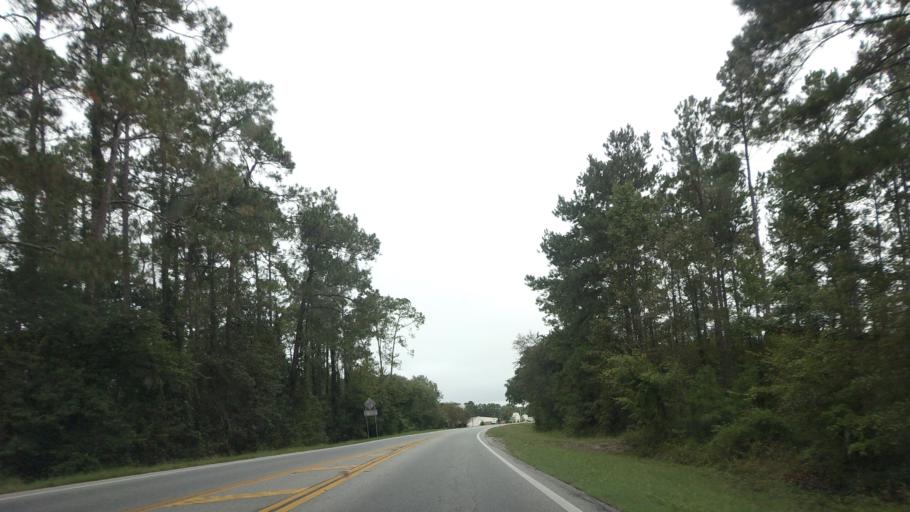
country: US
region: Georgia
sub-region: Berrien County
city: Nashville
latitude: 31.1915
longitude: -83.2497
